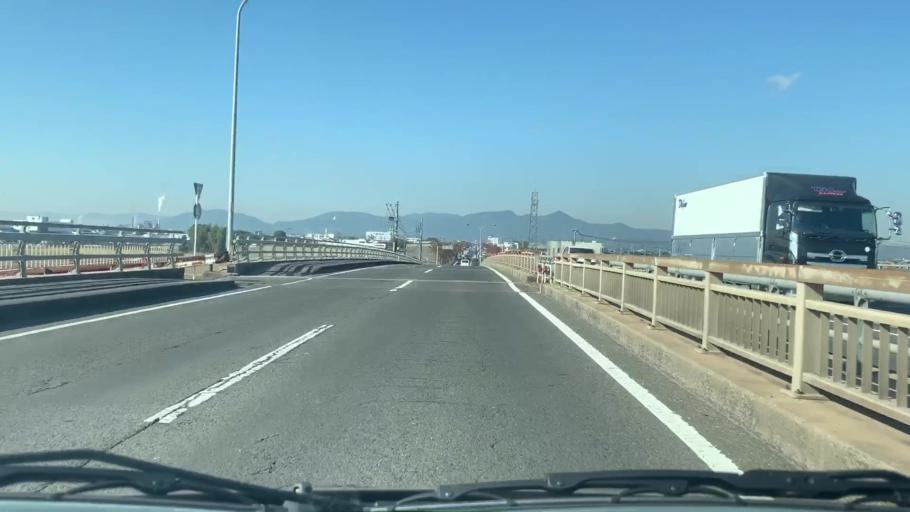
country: JP
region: Saga Prefecture
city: Saga-shi
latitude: 33.2644
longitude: 130.2426
